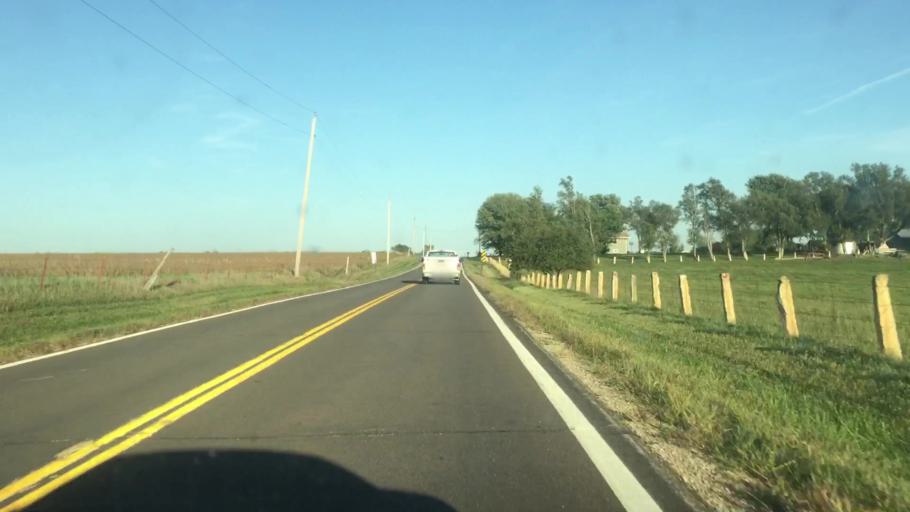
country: US
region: Kansas
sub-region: Brown County
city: Horton
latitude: 39.5517
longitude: -95.4520
